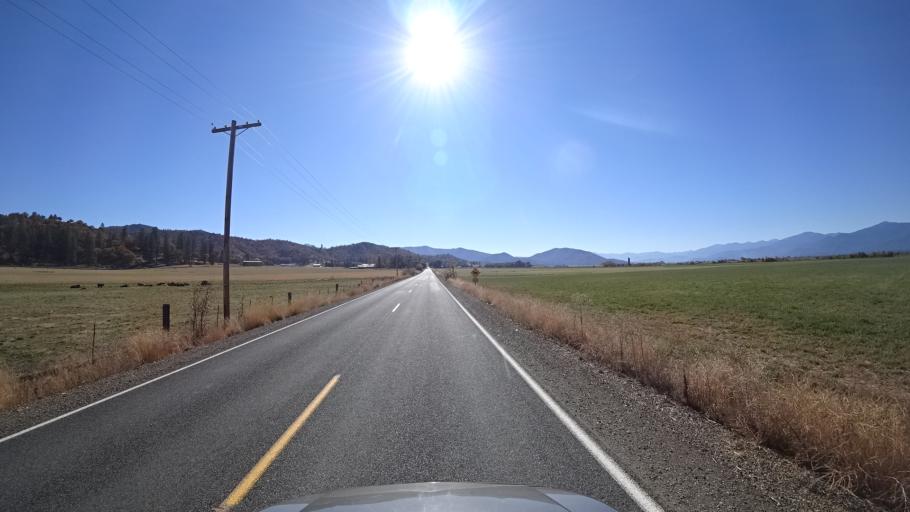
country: US
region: California
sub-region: Siskiyou County
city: Yreka
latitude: 41.5989
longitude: -122.8449
